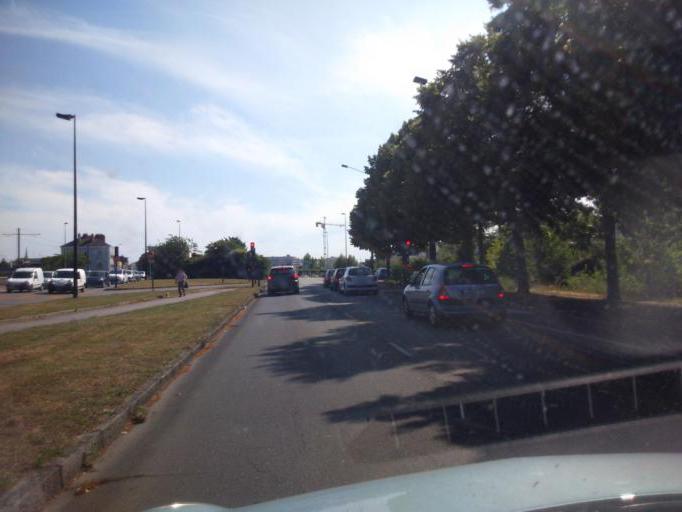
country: FR
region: Pays de la Loire
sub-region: Departement de la Loire-Atlantique
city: Reze
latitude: 47.1962
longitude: -1.5438
